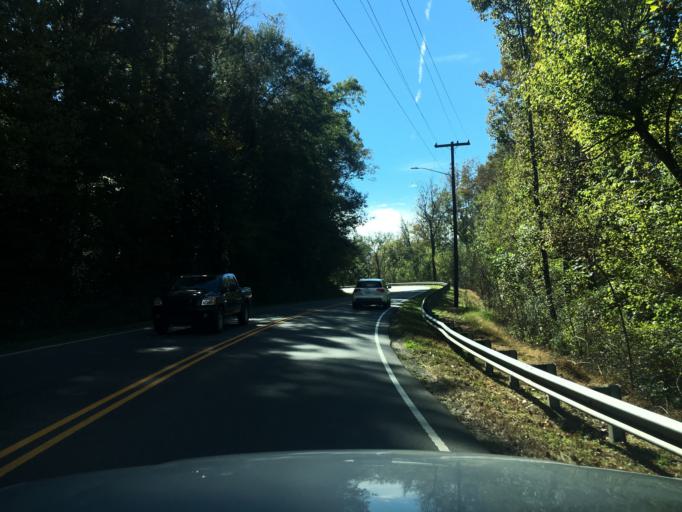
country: US
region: North Carolina
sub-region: Burke County
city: Morganton
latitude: 35.7415
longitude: -81.7097
